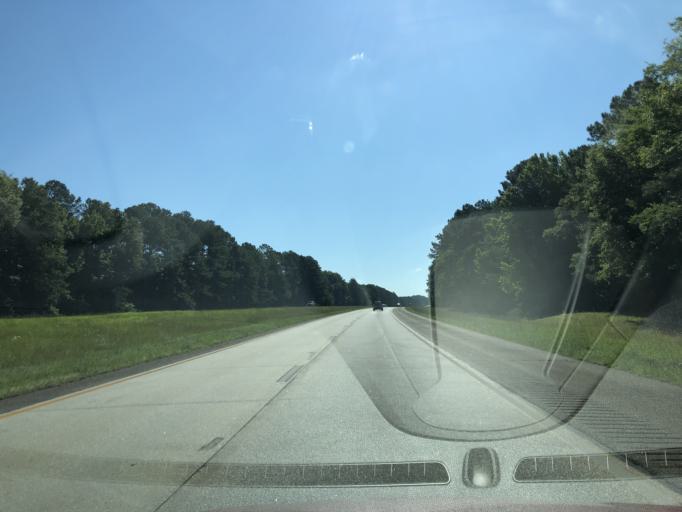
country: US
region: Georgia
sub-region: Warren County
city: Firing Range
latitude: 33.5031
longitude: -82.7700
